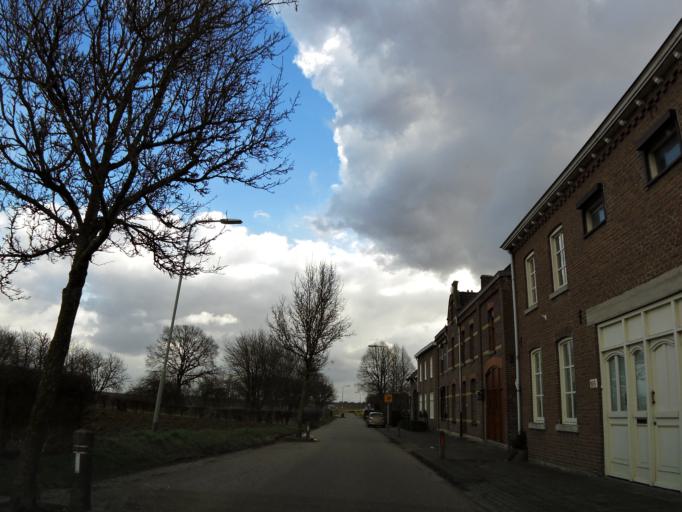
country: NL
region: Limburg
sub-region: Gemeente Onderbanken
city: Merkelbeek
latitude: 50.9668
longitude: 5.9449
